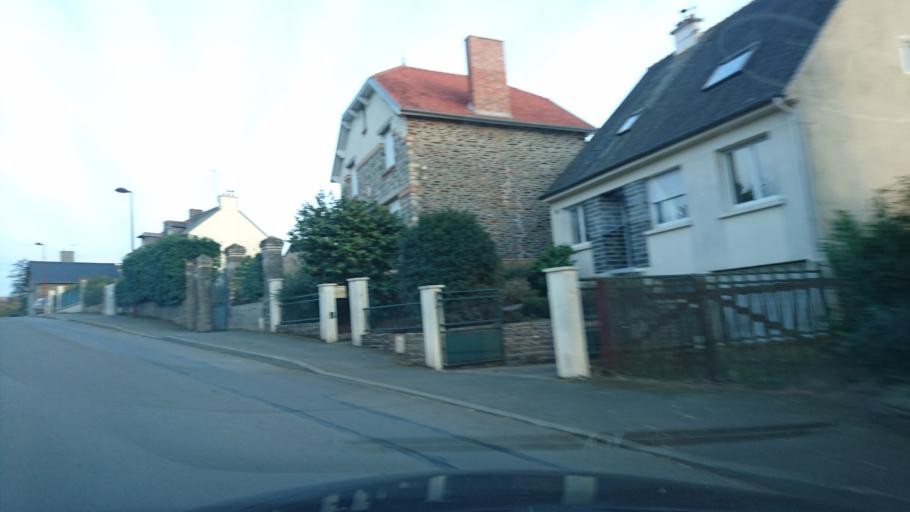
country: FR
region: Brittany
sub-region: Departement du Morbihan
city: Guer
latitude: 47.8760
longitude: -2.0851
